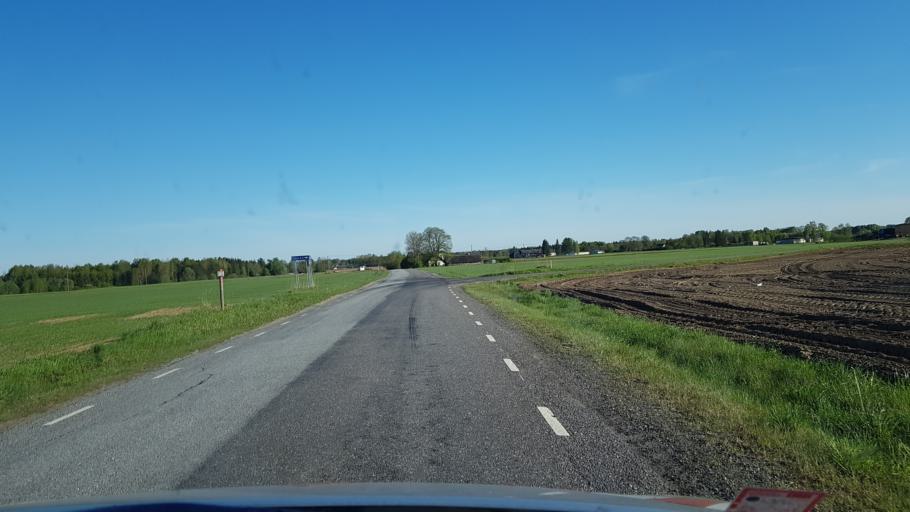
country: EE
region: Vorumaa
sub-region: Voru linn
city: Voru
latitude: 57.9220
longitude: 26.9510
